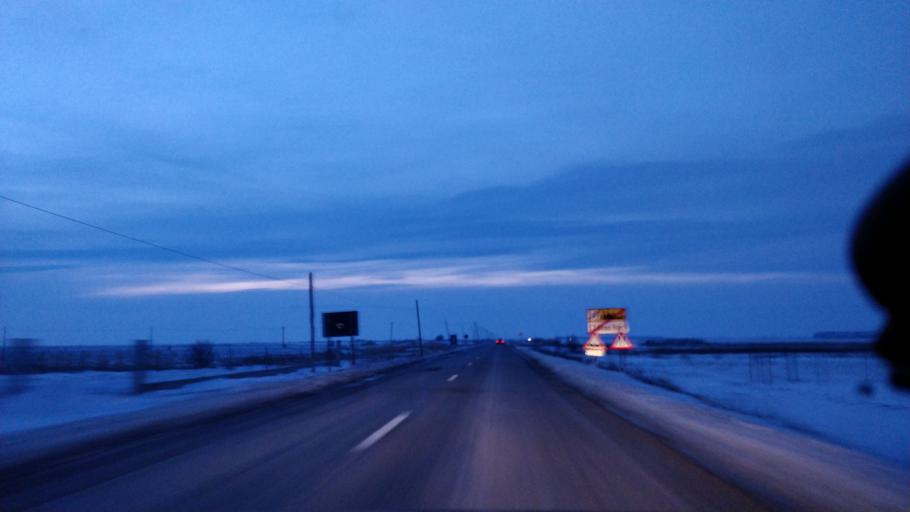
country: RO
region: Galati
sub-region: Comuna Liesti
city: Liesti
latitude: 45.5906
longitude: 27.4844
